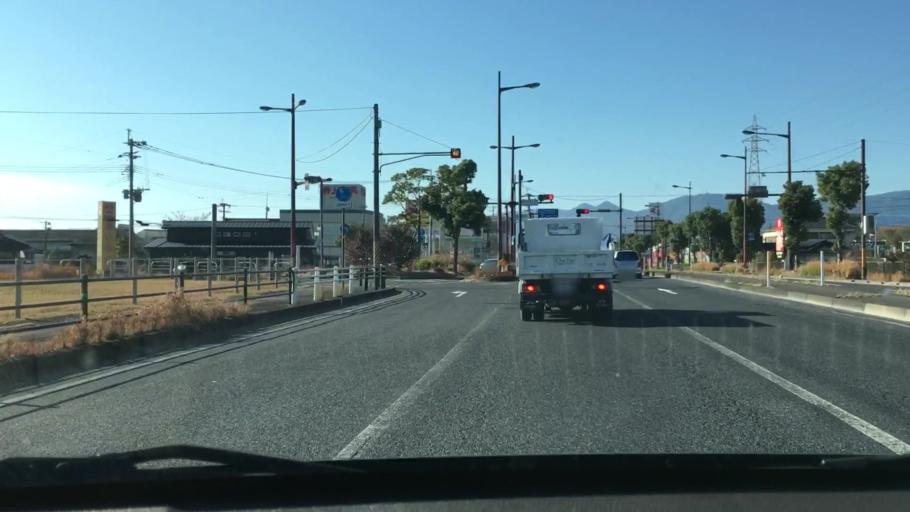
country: JP
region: Kagoshima
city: Kajiki
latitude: 31.7376
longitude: 130.6502
